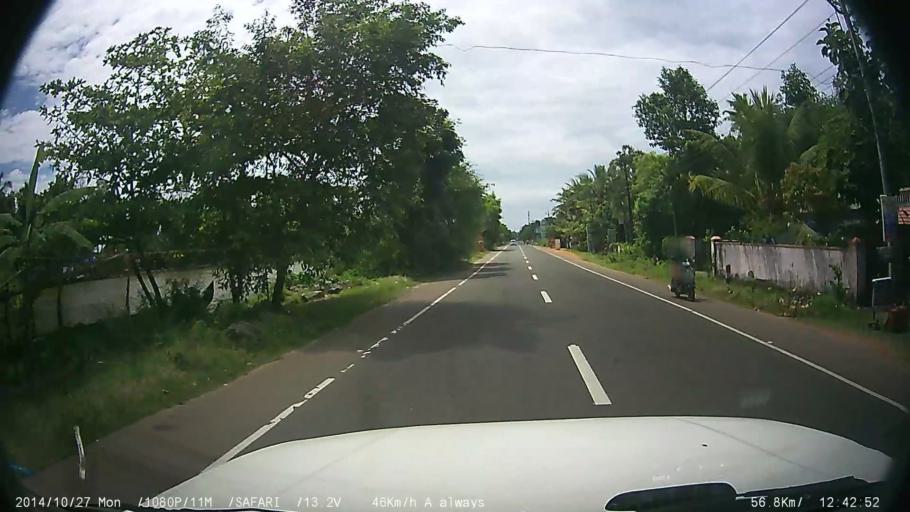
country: IN
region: Kerala
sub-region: Kottayam
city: Changanacheri
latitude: 9.4235
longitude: 76.5037
